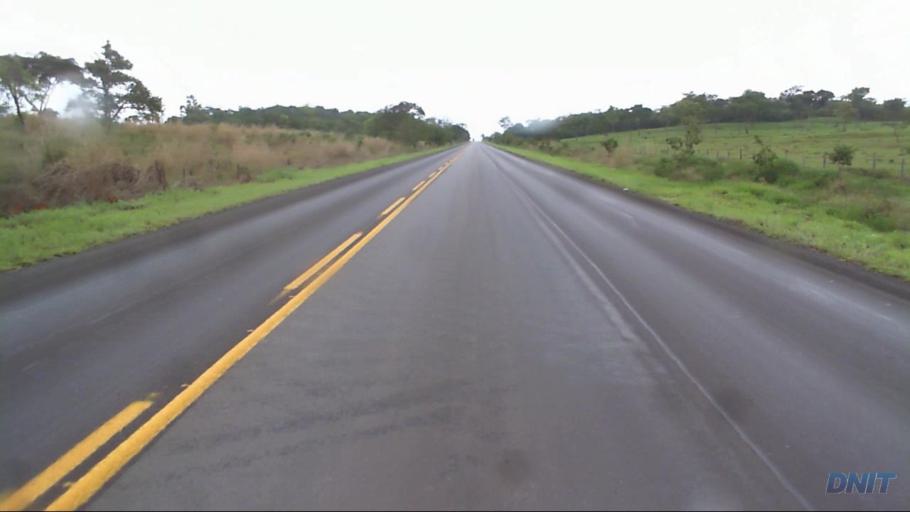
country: BR
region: Goias
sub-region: Padre Bernardo
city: Padre Bernardo
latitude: -15.2069
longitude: -48.4659
